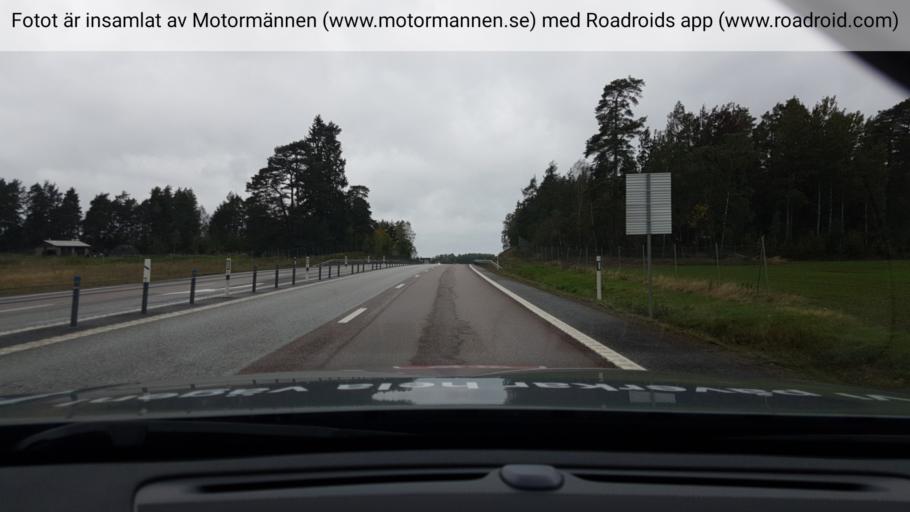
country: SE
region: Vaermland
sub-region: Kristinehamns Kommun
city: Kristinehamn
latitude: 59.3757
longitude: 13.9310
